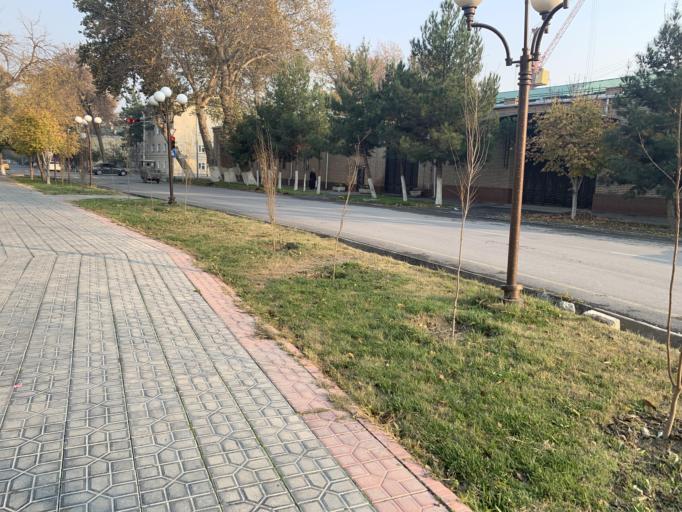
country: UZ
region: Fergana
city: Qo`qon
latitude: 40.5362
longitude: 70.9363
